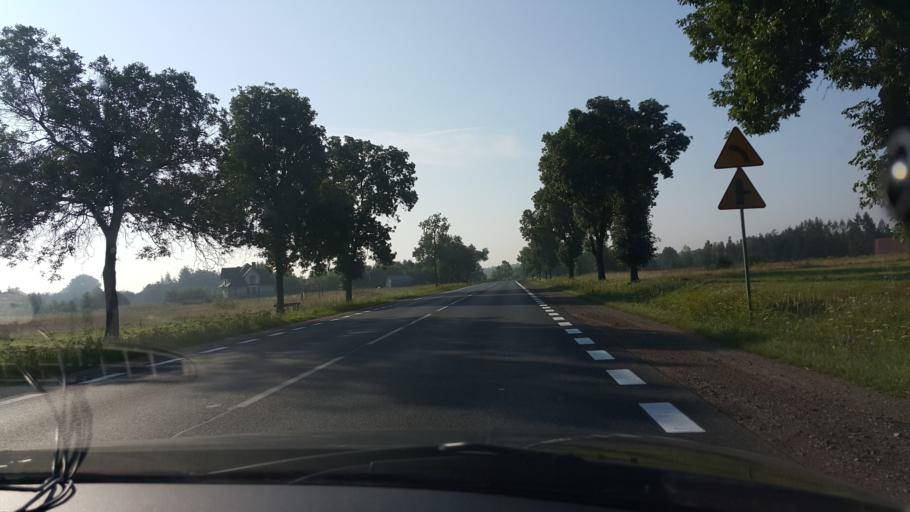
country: PL
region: Masovian Voivodeship
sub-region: Powiat radomski
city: Jedlnia-Letnisko
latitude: 51.3913
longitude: 21.2726
